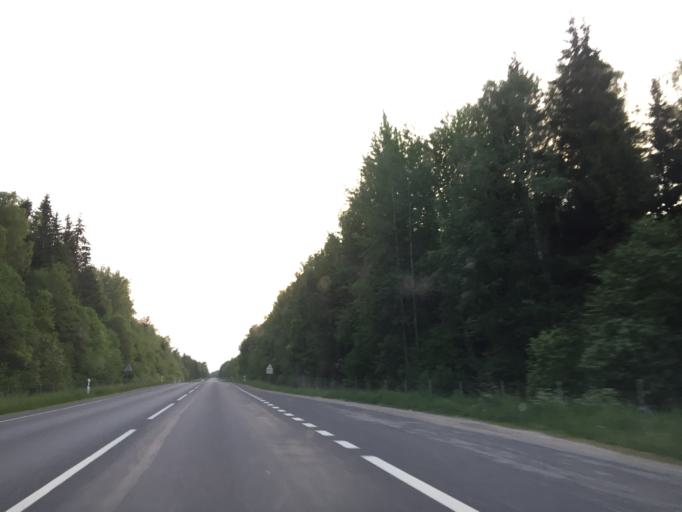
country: LT
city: Kursenai
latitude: 55.9999
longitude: 22.8185
